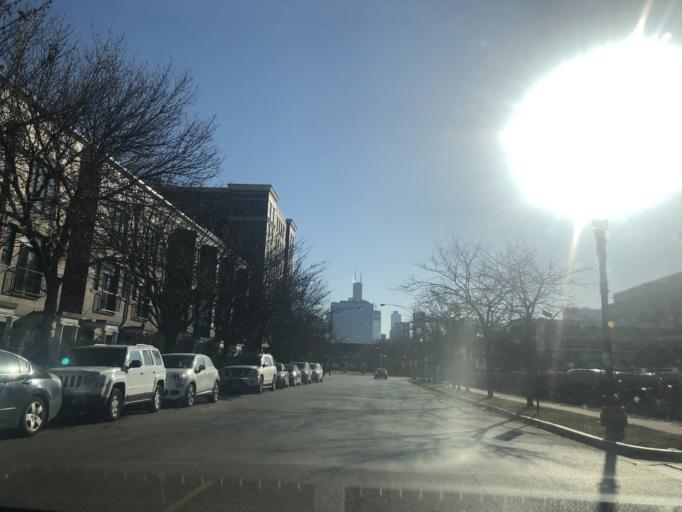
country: US
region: Illinois
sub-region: Cook County
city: Chicago
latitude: 41.9049
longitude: -87.6384
